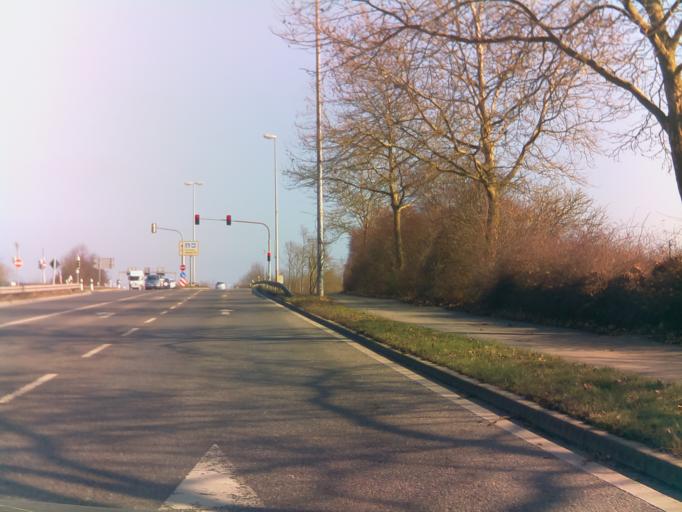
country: DE
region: Baden-Wuerttemberg
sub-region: Regierungsbezirk Stuttgart
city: Ehningen
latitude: 48.6886
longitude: 8.9653
